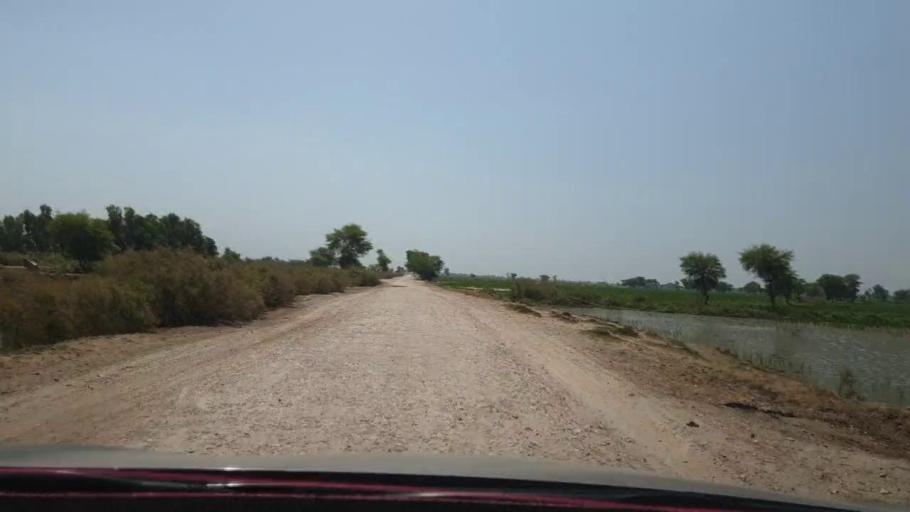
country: PK
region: Sindh
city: Kambar
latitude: 27.5707
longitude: 67.8805
